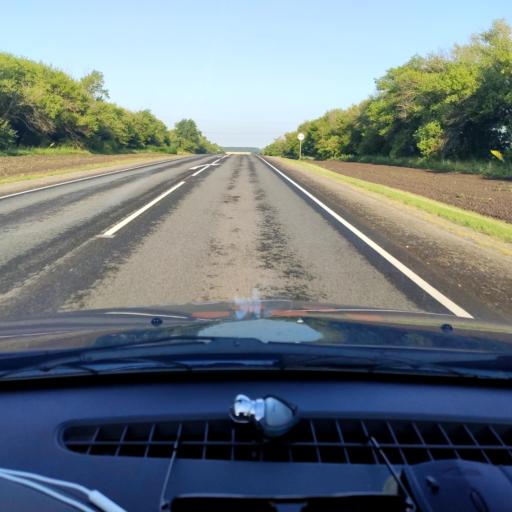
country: RU
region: Orjol
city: Livny
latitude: 52.4297
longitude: 37.7909
